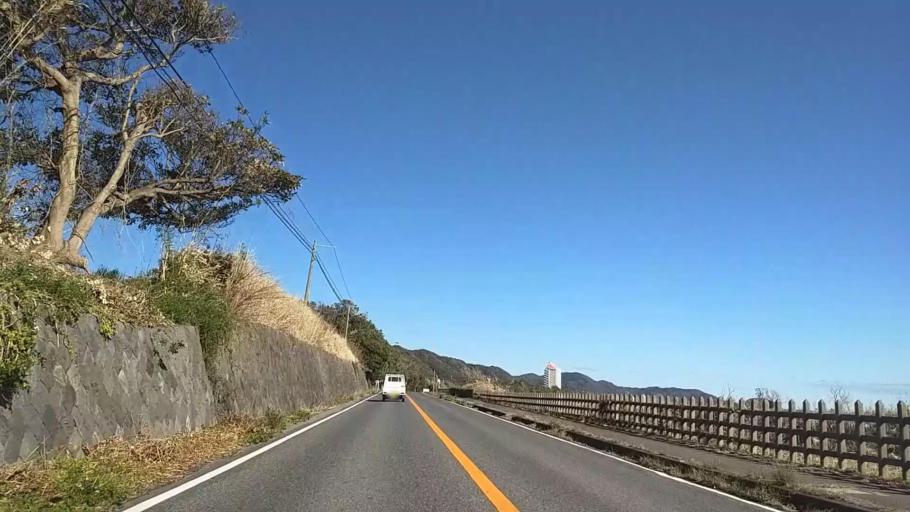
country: JP
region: Chiba
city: Kawaguchi
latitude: 35.0458
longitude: 140.0251
